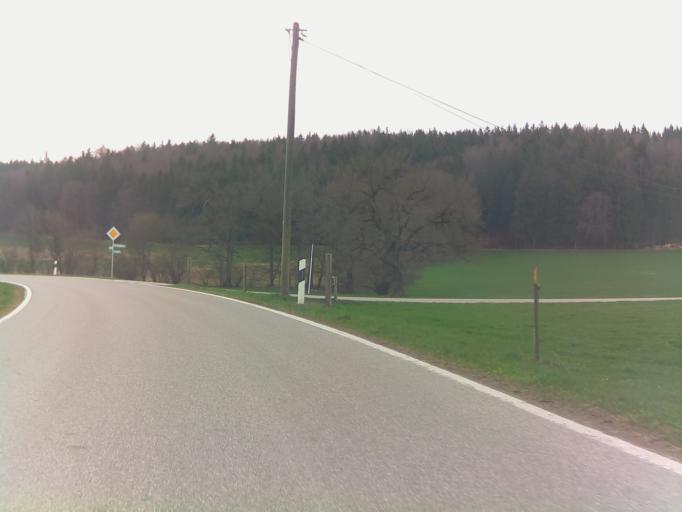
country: DE
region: Bavaria
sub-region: Upper Bavaria
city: Obersochering
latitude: 47.7616
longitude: 11.2291
